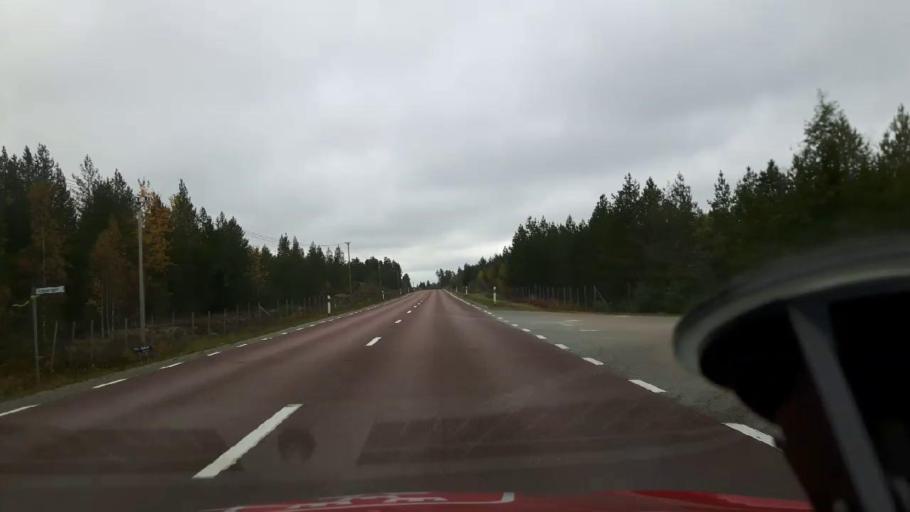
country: SE
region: Jaemtland
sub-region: Harjedalens Kommun
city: Sveg
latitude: 62.2472
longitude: 14.8252
